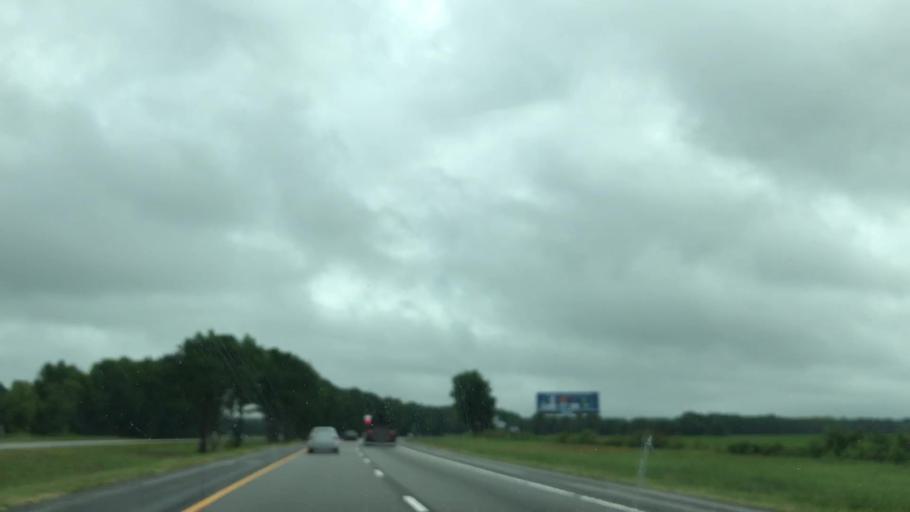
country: US
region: North Carolina
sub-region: Halifax County
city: Enfield
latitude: 36.1577
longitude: -77.7824
